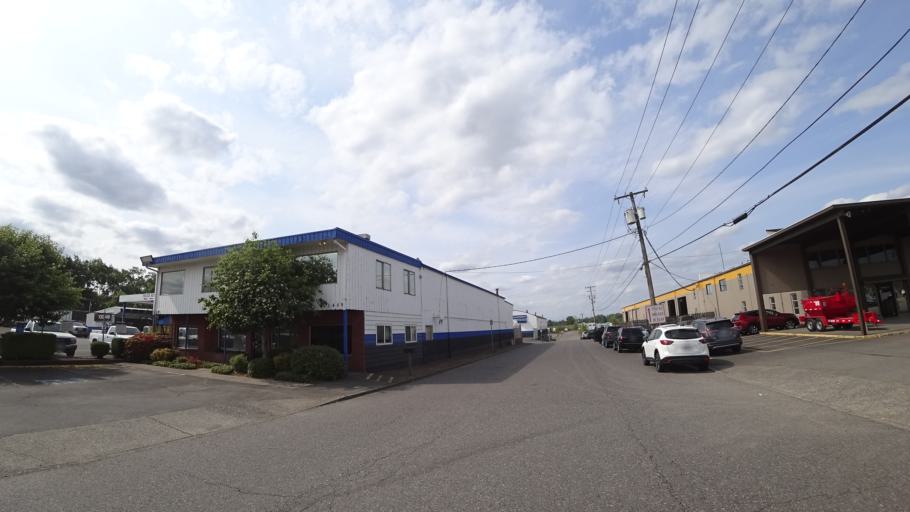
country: US
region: Oregon
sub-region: Multnomah County
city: Portland
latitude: 45.5784
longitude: -122.6503
